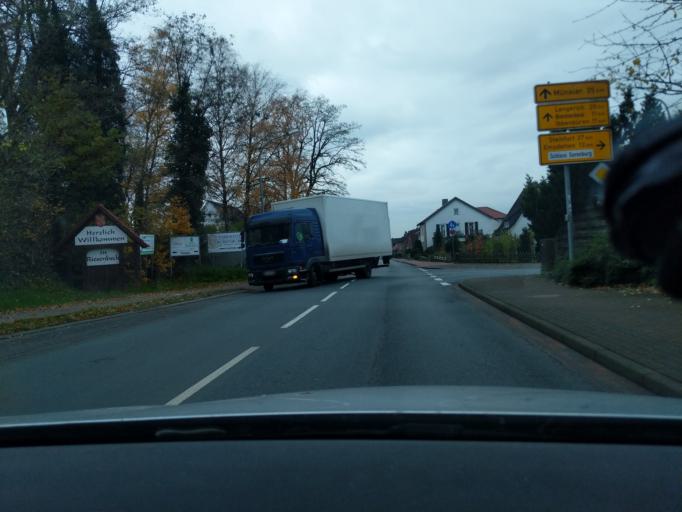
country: DE
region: North Rhine-Westphalia
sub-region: Regierungsbezirk Munster
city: Birgte
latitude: 52.2625
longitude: 7.6221
